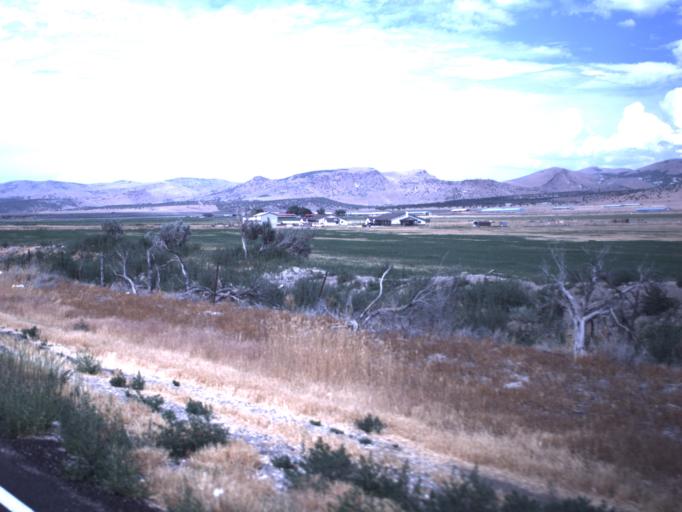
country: US
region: Utah
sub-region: Sanpete County
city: Fountain Green
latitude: 39.5790
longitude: -111.6112
